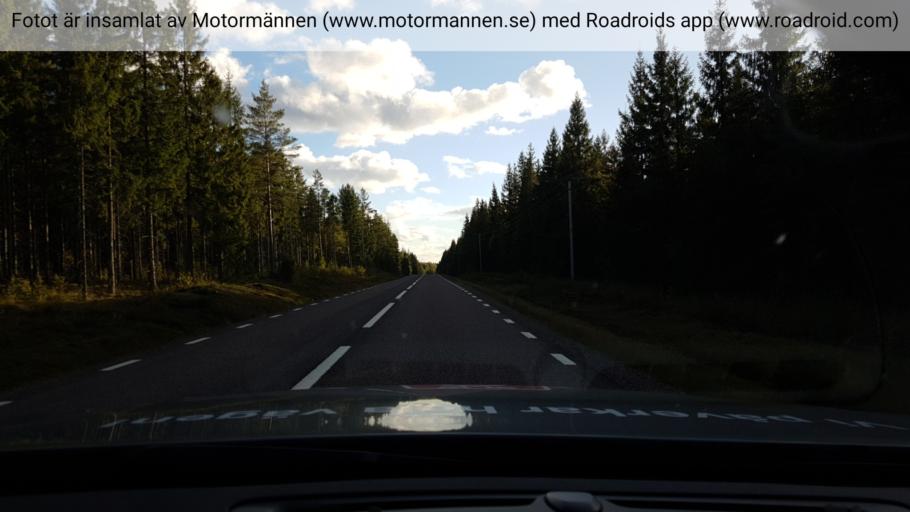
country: SE
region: Vaermland
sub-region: Karlstads Kommun
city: Molkom
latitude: 59.7638
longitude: 13.6985
